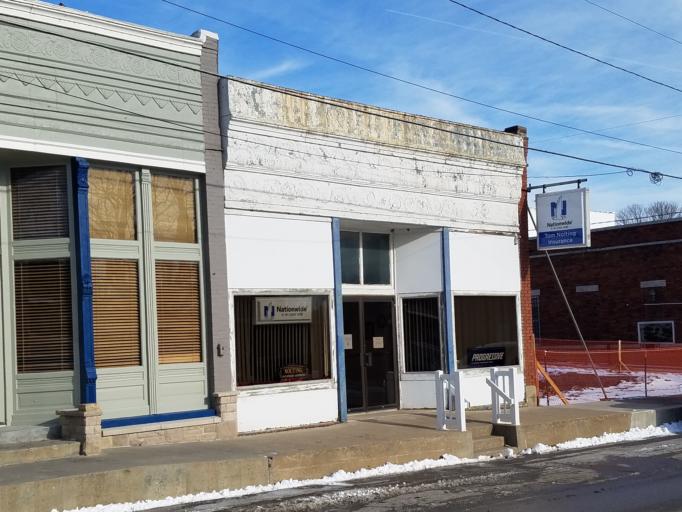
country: US
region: Missouri
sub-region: Lafayette County
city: Lexington
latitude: 39.1338
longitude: -93.9837
